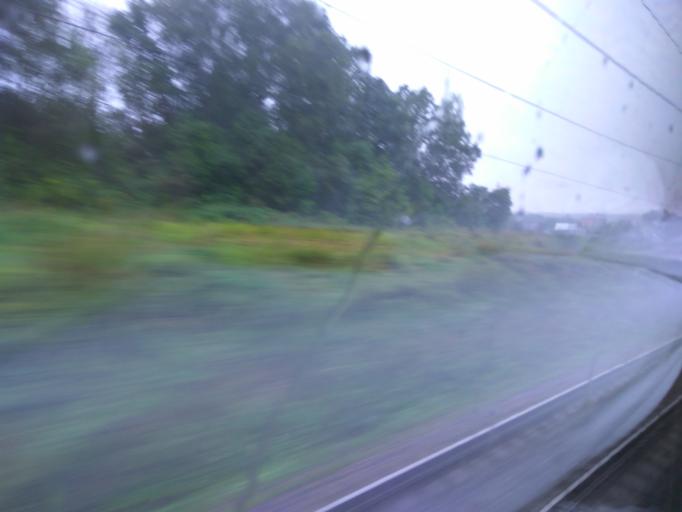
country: RU
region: Moskovskaya
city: Ozherel'ye
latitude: 54.8280
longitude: 38.2481
